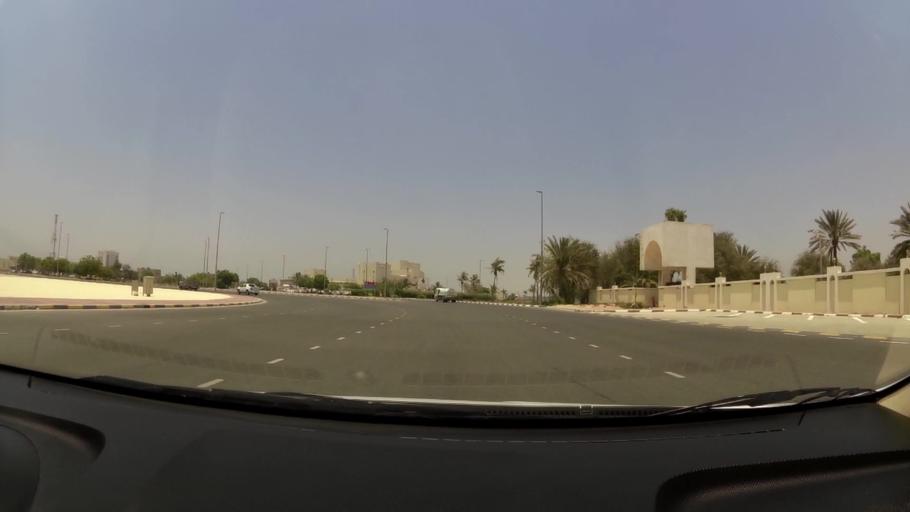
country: AE
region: Umm al Qaywayn
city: Umm al Qaywayn
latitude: 25.5729
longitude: 55.5660
